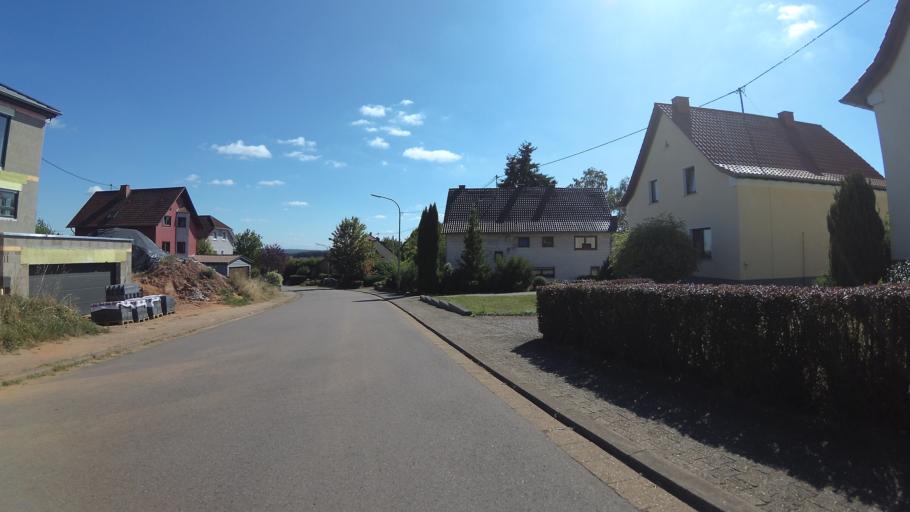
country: DE
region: Saarland
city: Lebach
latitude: 49.3830
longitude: 6.8858
